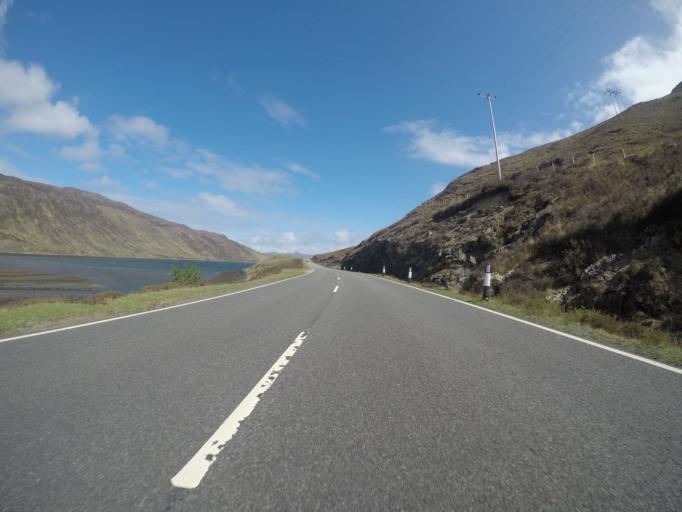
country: GB
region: Scotland
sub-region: Highland
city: Isle of Skye
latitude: 57.2993
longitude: -6.1474
